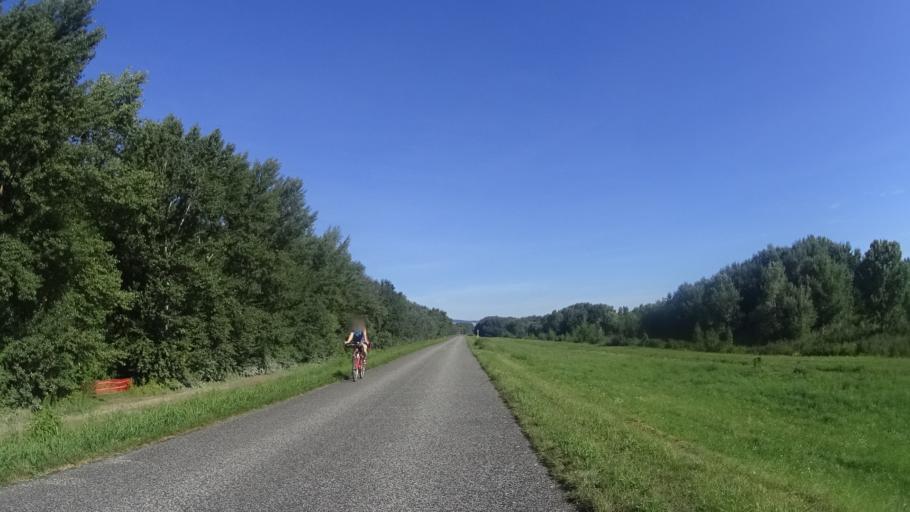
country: SK
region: Bratislavsky
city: Bratislava
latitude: 48.0922
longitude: 17.1532
